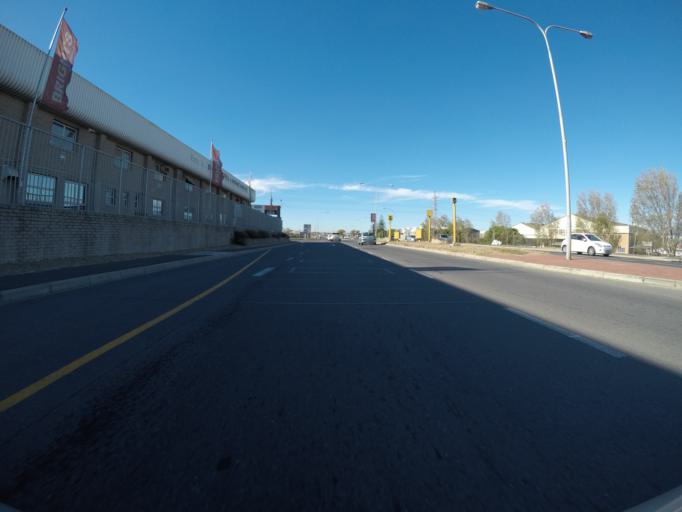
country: ZA
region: Western Cape
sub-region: City of Cape Town
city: Kraaifontein
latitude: -33.8974
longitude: 18.6712
